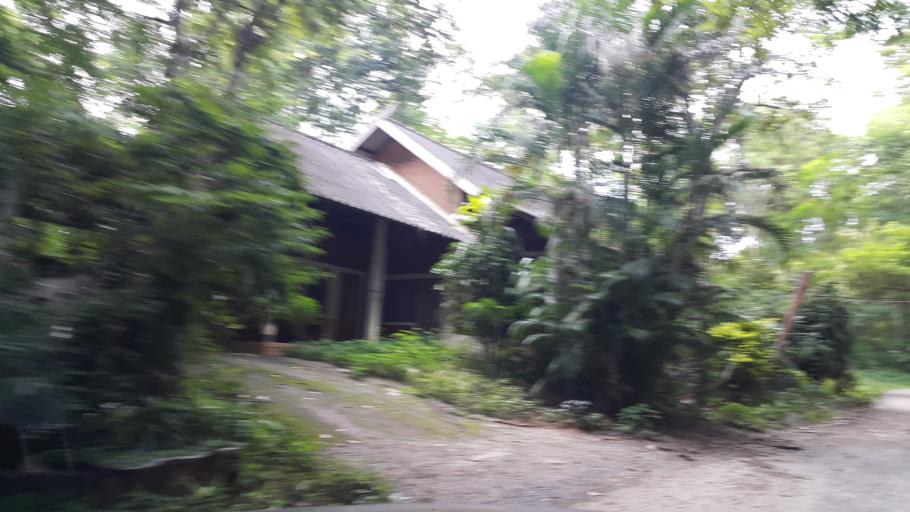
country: TH
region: Chiang Mai
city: Mae On
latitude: 18.8886
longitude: 99.2203
